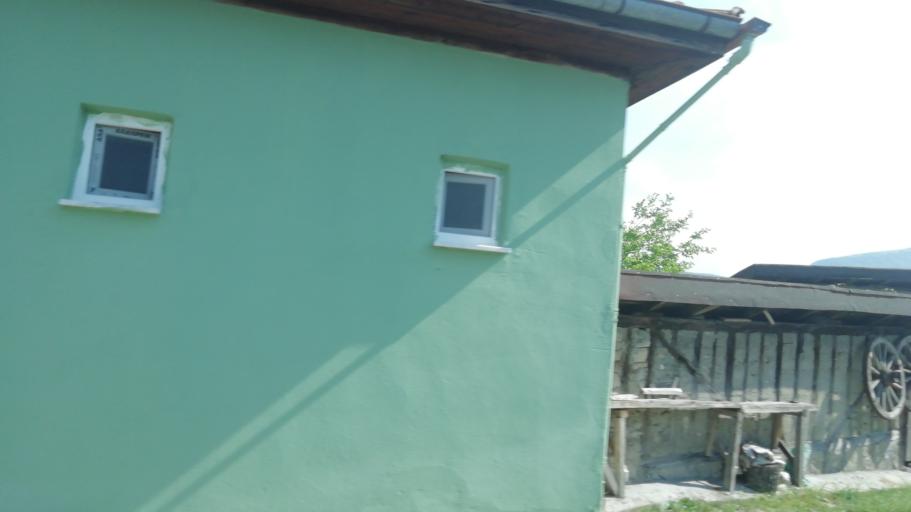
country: TR
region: Karabuk
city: Karabuk
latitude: 41.1162
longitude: 32.5744
